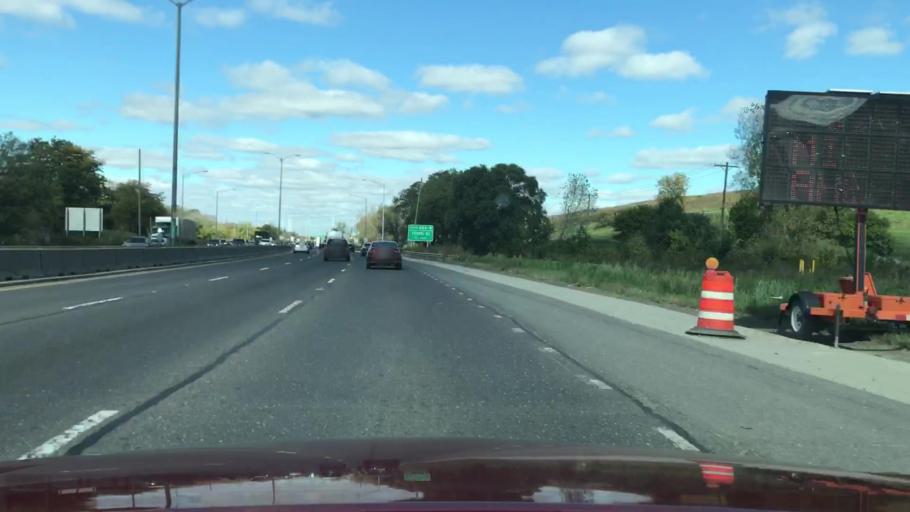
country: US
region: Illinois
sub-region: Cook County
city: Burnham
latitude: 41.6502
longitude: -87.5803
